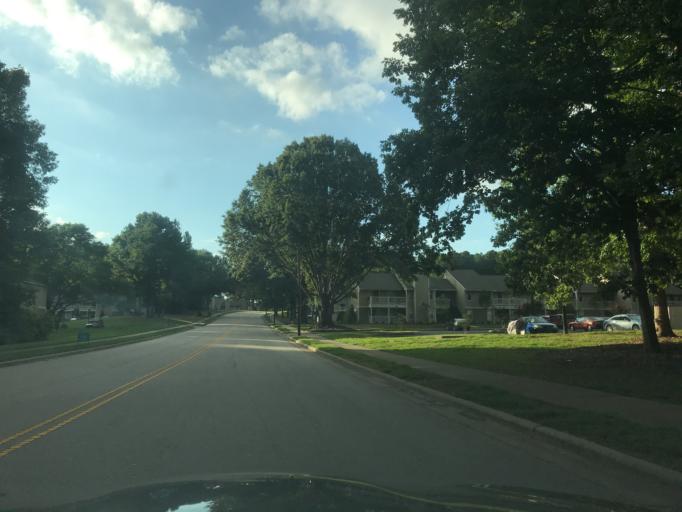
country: US
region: North Carolina
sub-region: Wake County
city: West Raleigh
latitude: 35.8635
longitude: -78.6304
